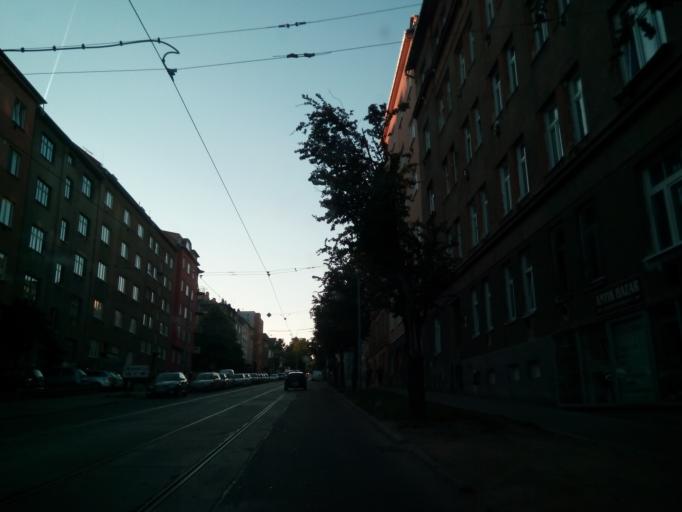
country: CZ
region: South Moravian
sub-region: Mesto Brno
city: Brno
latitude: 49.2048
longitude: 16.6236
